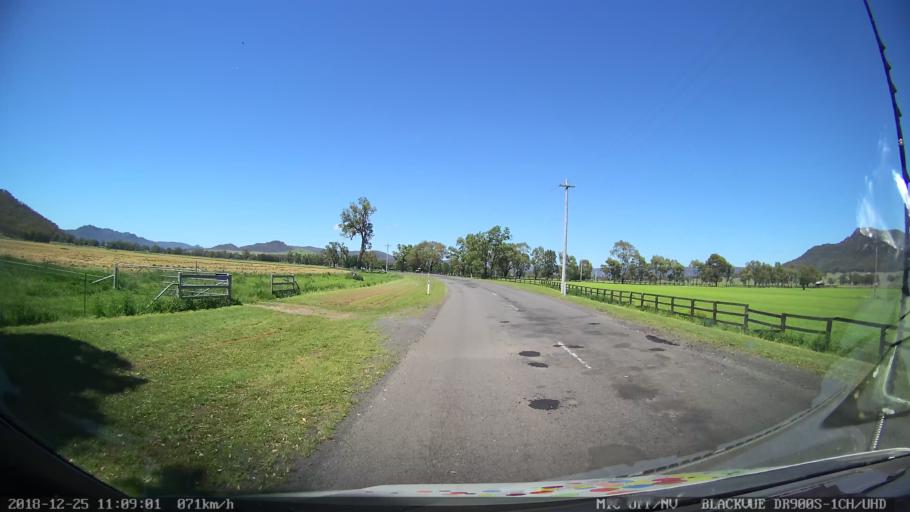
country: AU
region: New South Wales
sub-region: Upper Hunter Shire
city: Merriwa
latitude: -32.4072
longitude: 150.1202
